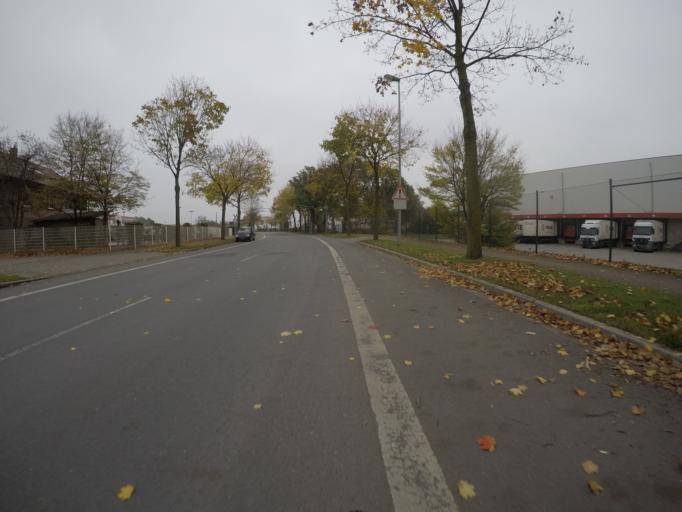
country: DE
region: North Rhine-Westphalia
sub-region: Regierungsbezirk Dusseldorf
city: Bocholt
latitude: 51.8113
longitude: 6.5462
